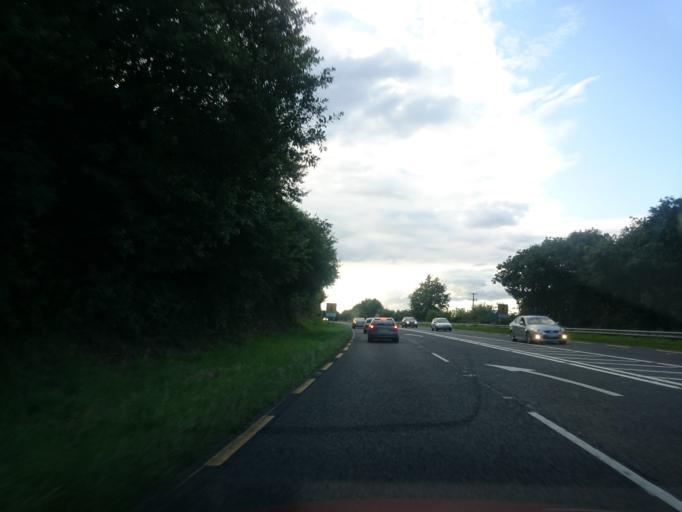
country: IE
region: Leinster
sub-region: Loch Garman
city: Loch Garman
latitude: 52.3599
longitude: -6.5082
